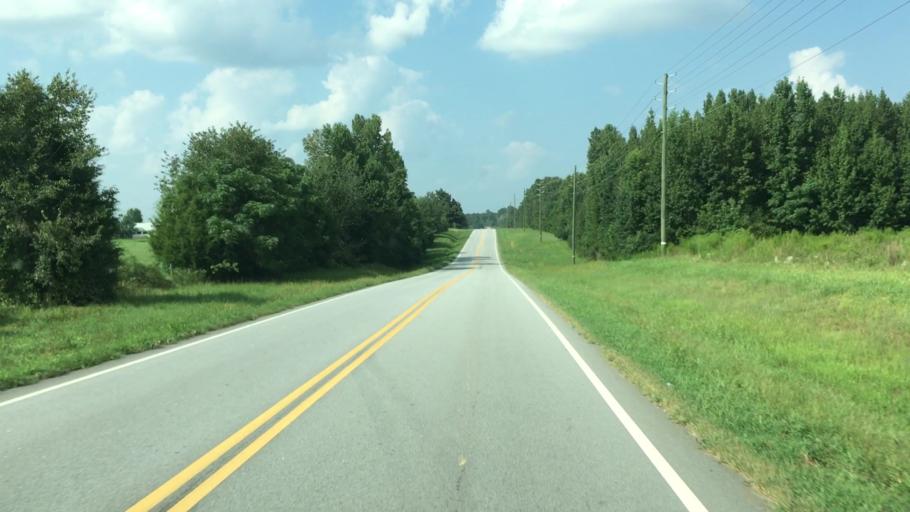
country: US
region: Georgia
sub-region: Jasper County
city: Monticello
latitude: 33.4440
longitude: -83.7570
